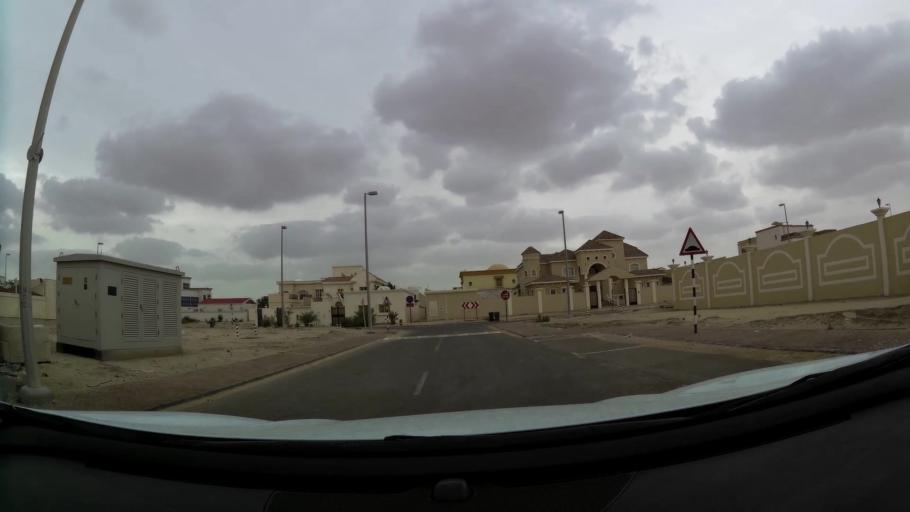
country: AE
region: Abu Dhabi
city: Abu Dhabi
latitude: 24.3720
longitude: 54.6317
